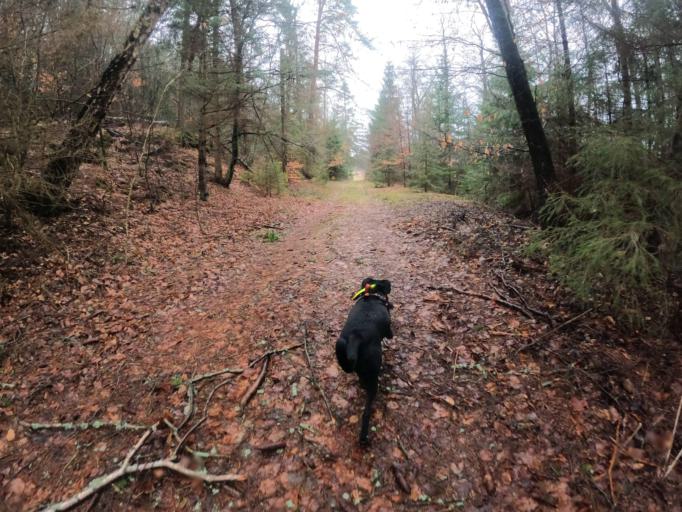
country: PL
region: West Pomeranian Voivodeship
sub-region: Powiat koszalinski
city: Polanow
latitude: 54.2352
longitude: 16.7194
